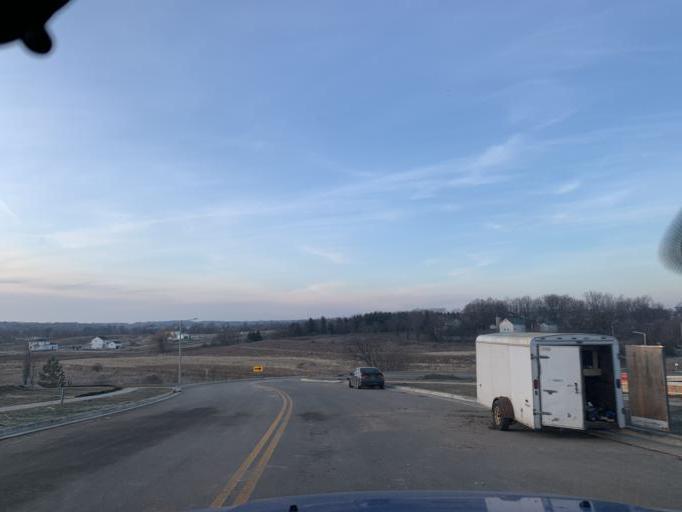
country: US
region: Wisconsin
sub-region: Dane County
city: Verona
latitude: 43.0477
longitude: -89.5594
